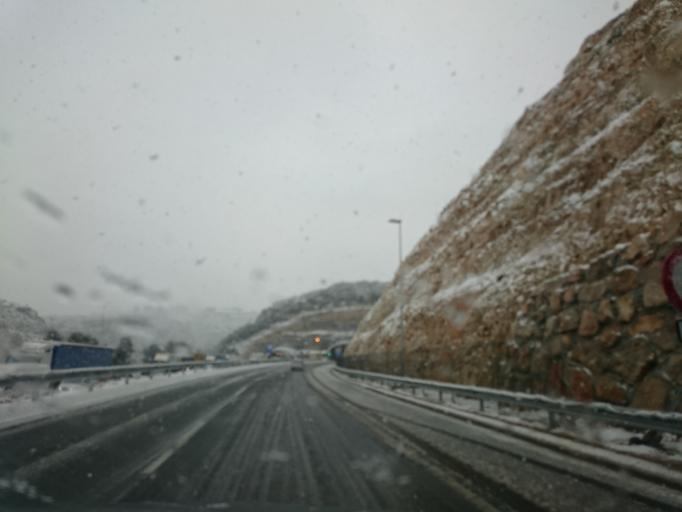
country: ES
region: Catalonia
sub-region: Provincia de Barcelona
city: Vilafranca del Penedes
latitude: 41.3027
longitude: 1.7241
